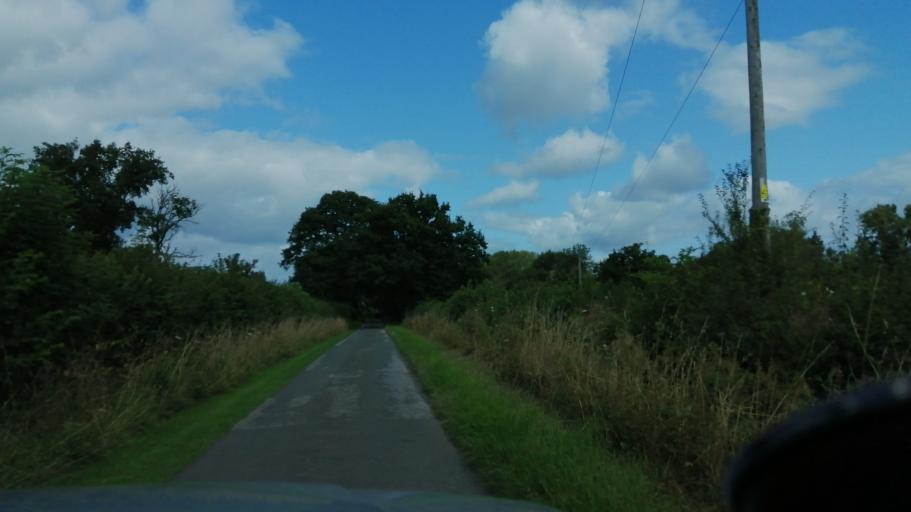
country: GB
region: England
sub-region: Herefordshire
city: Kinnersley
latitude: 52.1297
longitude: -2.9303
